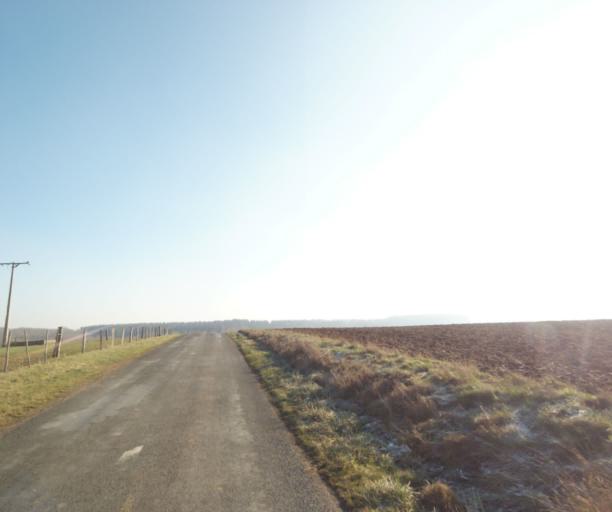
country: FR
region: Champagne-Ardenne
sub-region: Departement de la Haute-Marne
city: Bienville
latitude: 48.5025
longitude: 5.0411
